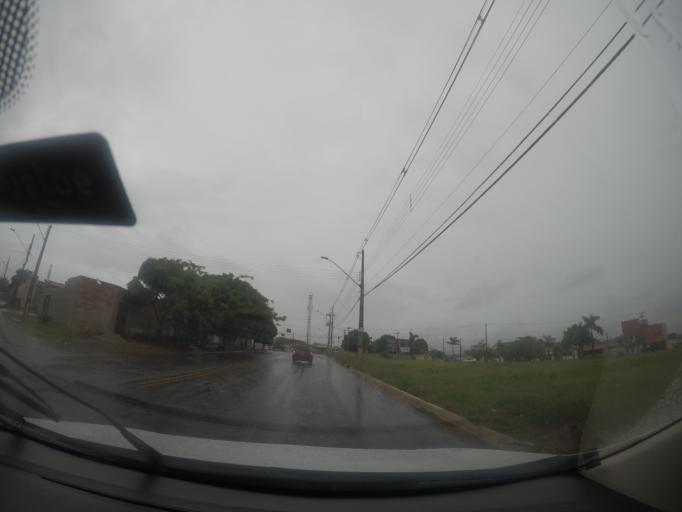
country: BR
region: Goias
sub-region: Goiania
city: Goiania
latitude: -16.6569
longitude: -49.3158
